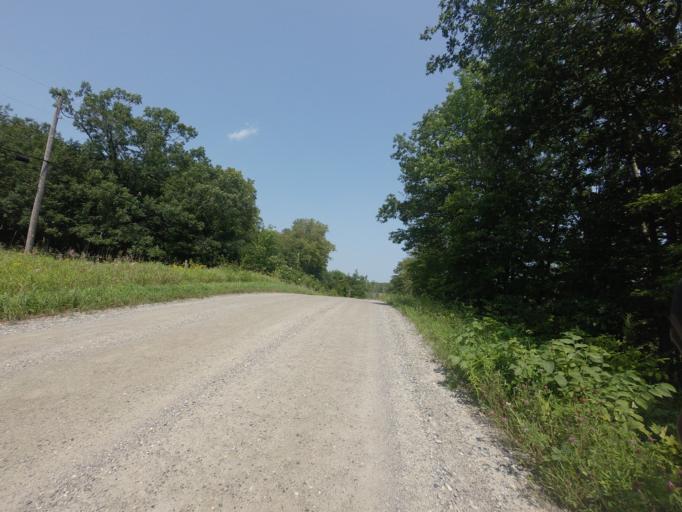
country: CA
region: Ontario
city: Kingston
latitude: 44.6473
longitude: -76.6864
